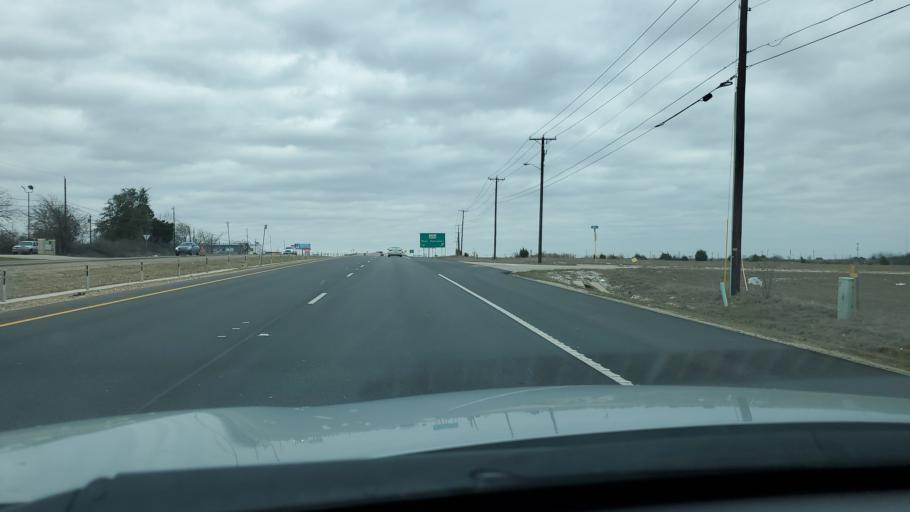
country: US
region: Texas
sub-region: Bell County
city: Killeen
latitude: 31.0727
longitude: -97.7603
